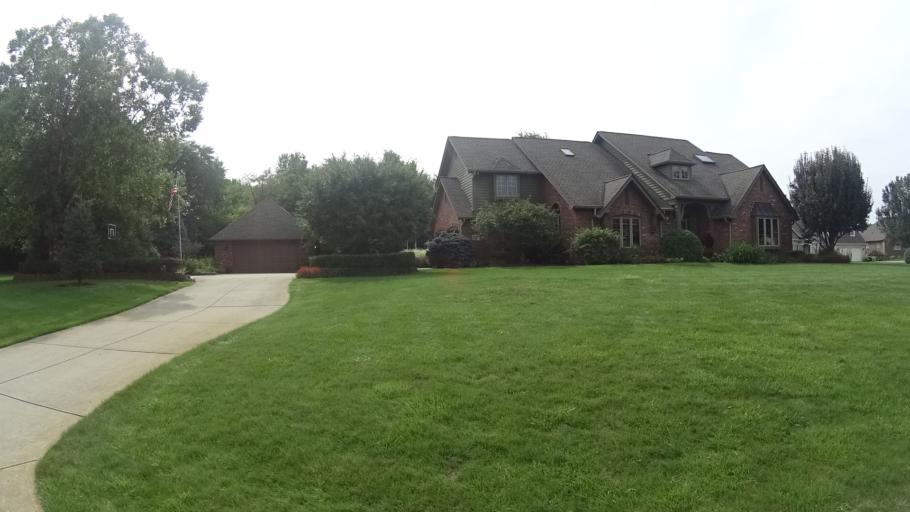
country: US
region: Indiana
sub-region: Madison County
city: Pendleton
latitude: 40.0129
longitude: -85.7876
